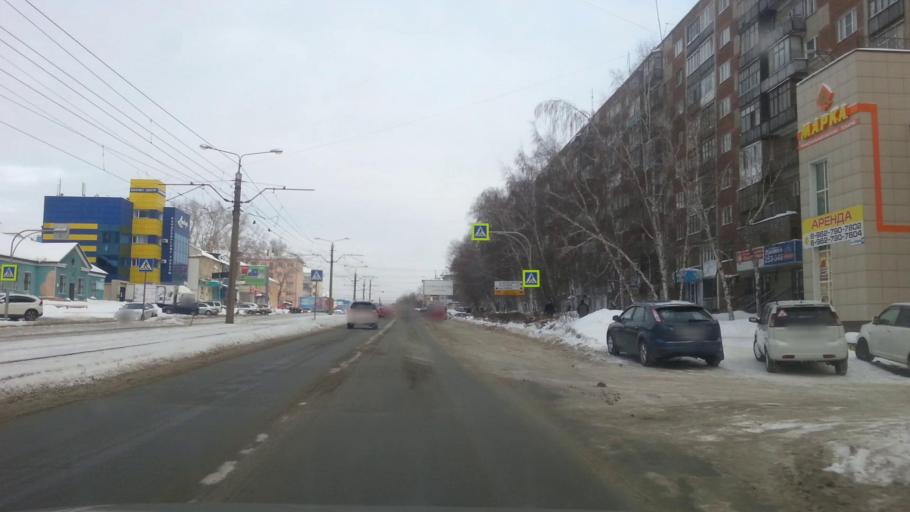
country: RU
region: Altai Krai
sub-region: Gorod Barnaulskiy
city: Barnaul
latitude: 53.3718
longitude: 83.7462
